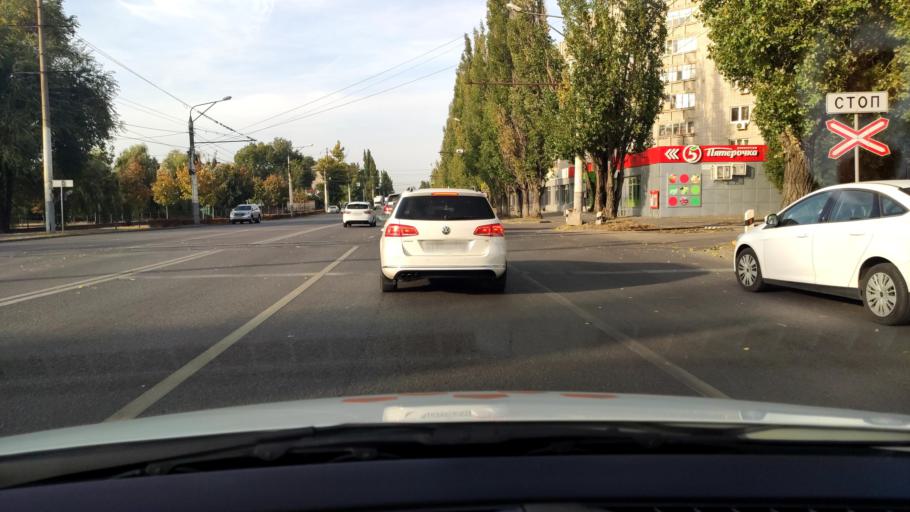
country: RU
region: Voronezj
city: Maslovka
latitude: 51.6060
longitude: 39.2372
